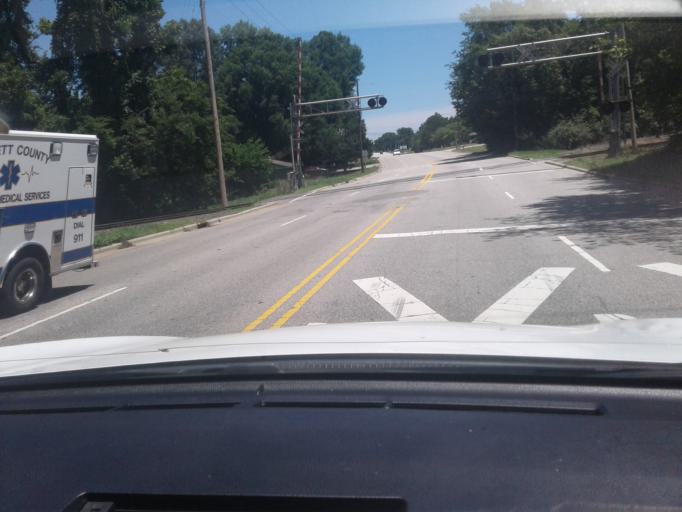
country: US
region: North Carolina
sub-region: Harnett County
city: Lillington
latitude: 35.3923
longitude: -78.8135
